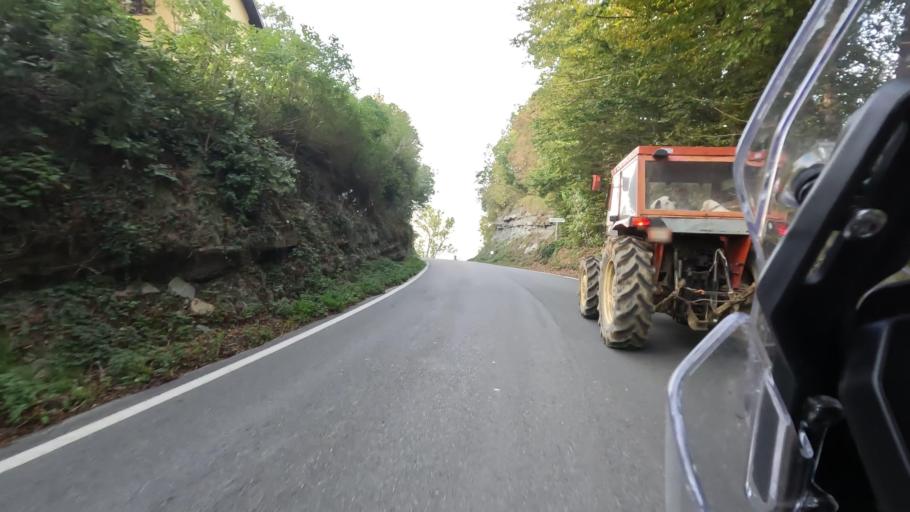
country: IT
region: Liguria
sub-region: Provincia di Savona
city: Sassello
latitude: 44.4865
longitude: 8.4972
